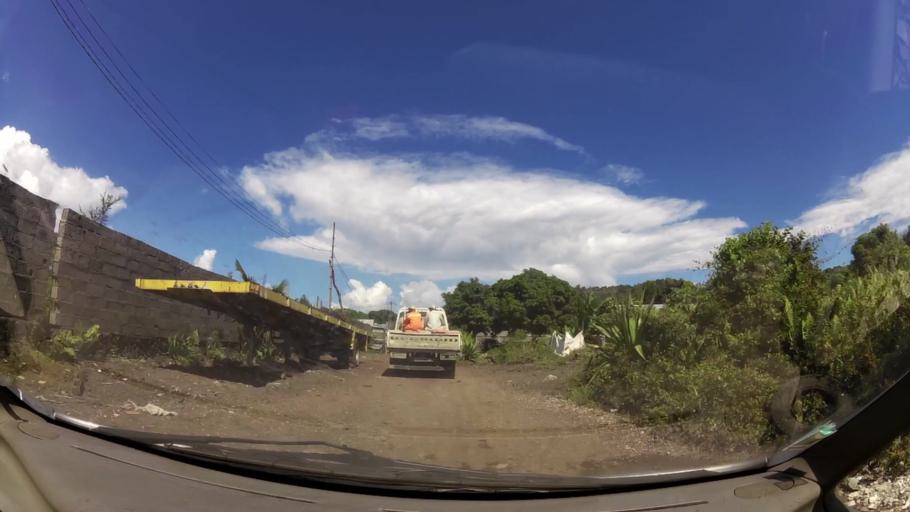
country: KM
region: Grande Comore
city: Mavingouni
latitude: -11.7294
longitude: 43.2415
